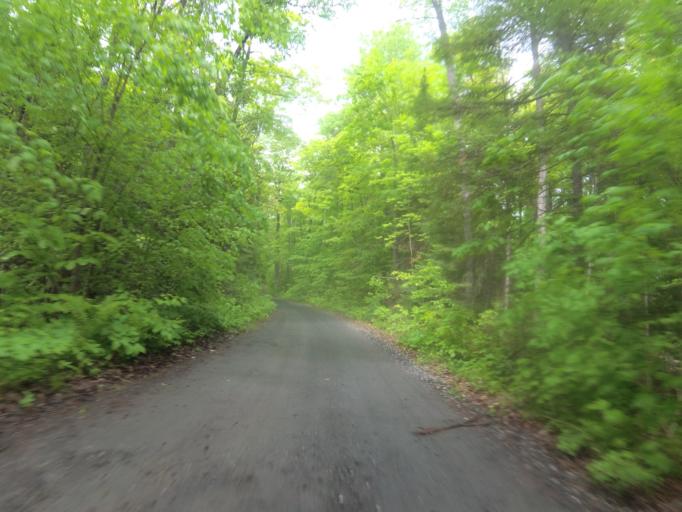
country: CA
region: Ontario
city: Renfrew
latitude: 45.1106
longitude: -76.8247
